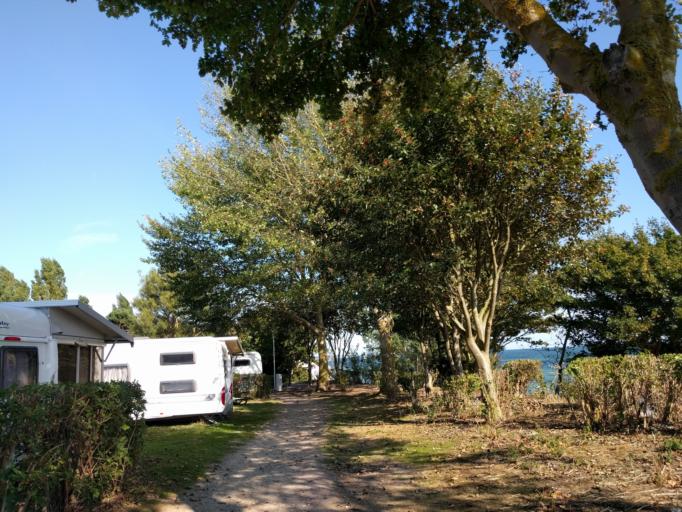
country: DE
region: Schleswig-Holstein
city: Burg auf Fehmarn
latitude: 54.4023
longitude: 11.1760
